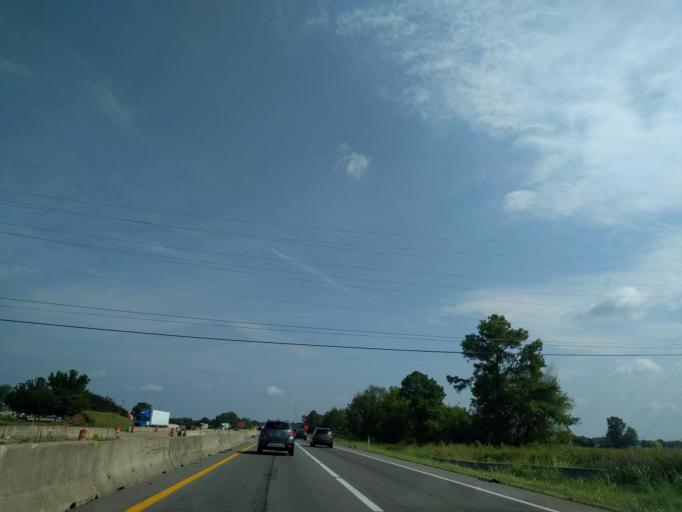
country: US
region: Tennessee
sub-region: Sumner County
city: Portland
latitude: 36.6335
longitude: -86.5728
